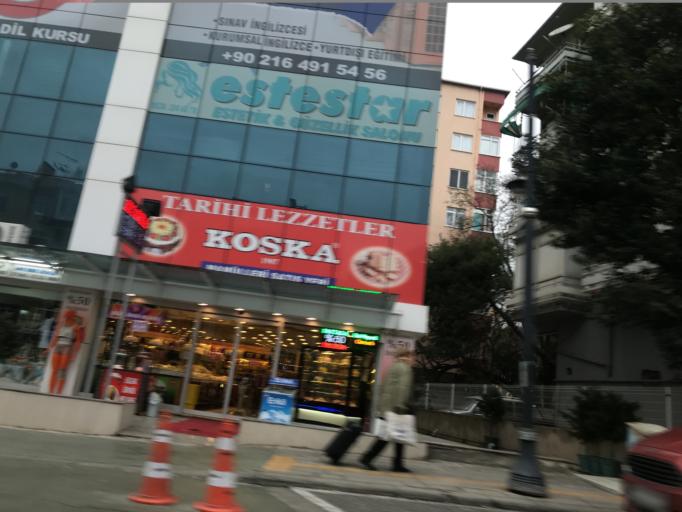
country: TR
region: Istanbul
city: Pendik
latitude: 40.8840
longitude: 29.2353
